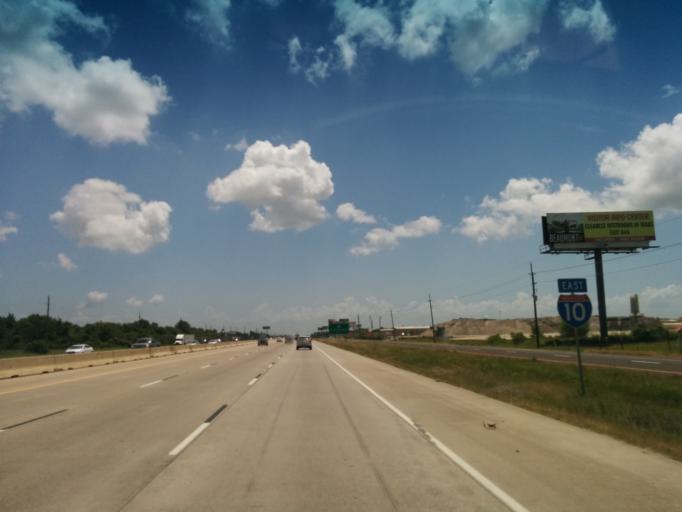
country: US
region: Texas
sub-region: Chambers County
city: Mont Belvieu
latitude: 29.8224
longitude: -94.8889
